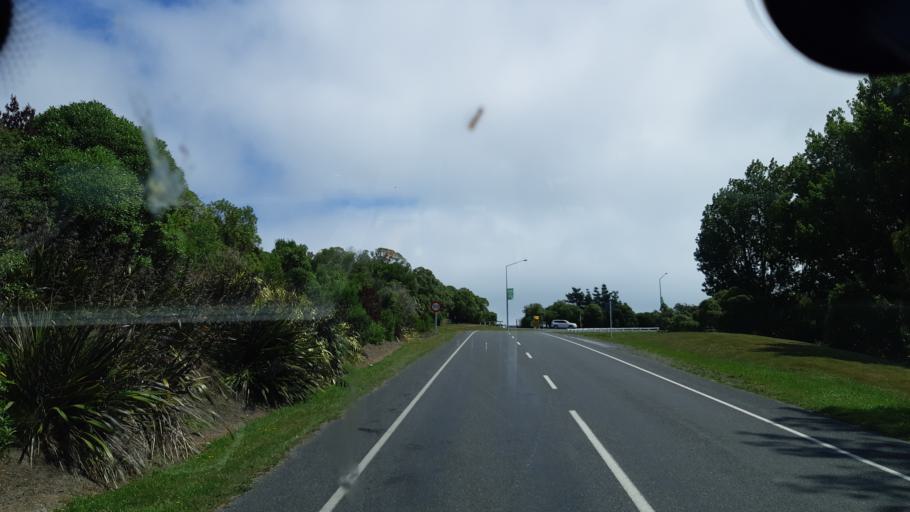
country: NZ
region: Canterbury
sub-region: Kaikoura District
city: Kaikoura
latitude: -42.4090
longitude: 173.6799
